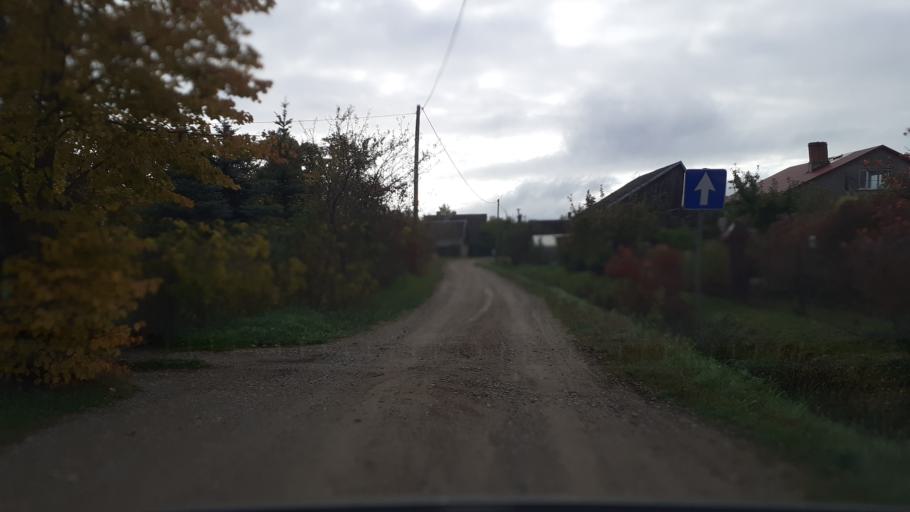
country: LV
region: Kuldigas Rajons
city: Kuldiga
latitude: 56.9650
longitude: 21.9917
